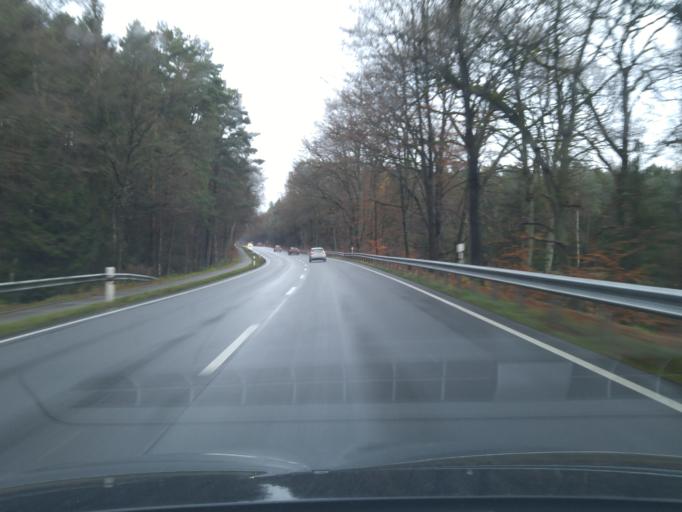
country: DE
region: Lower Saxony
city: Suderburg
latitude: 52.8785
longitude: 10.4998
